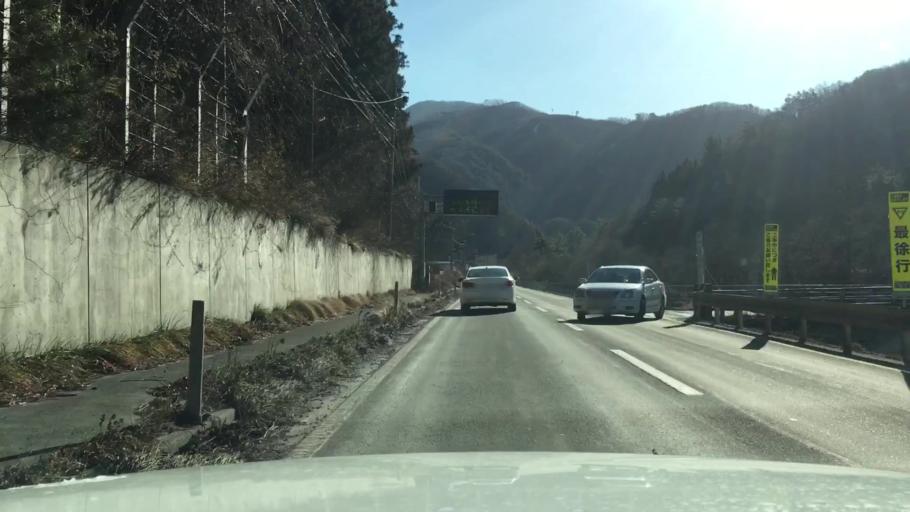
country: JP
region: Iwate
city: Miyako
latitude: 39.5957
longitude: 141.6594
